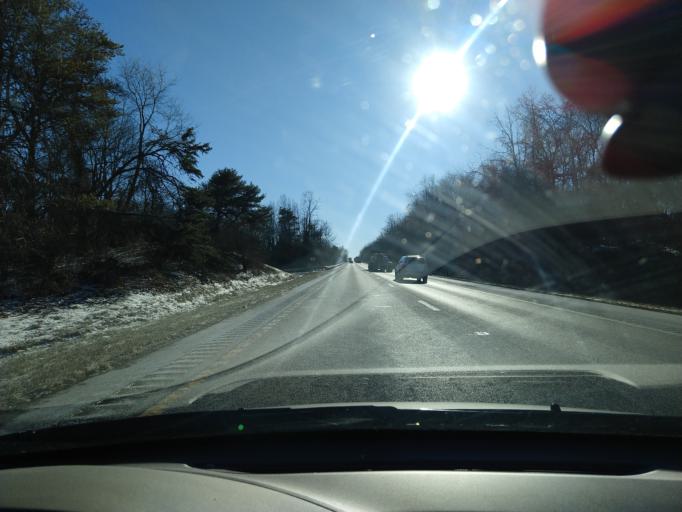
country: US
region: Virginia
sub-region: Botetourt County
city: Daleville
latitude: 37.4279
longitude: -79.8769
